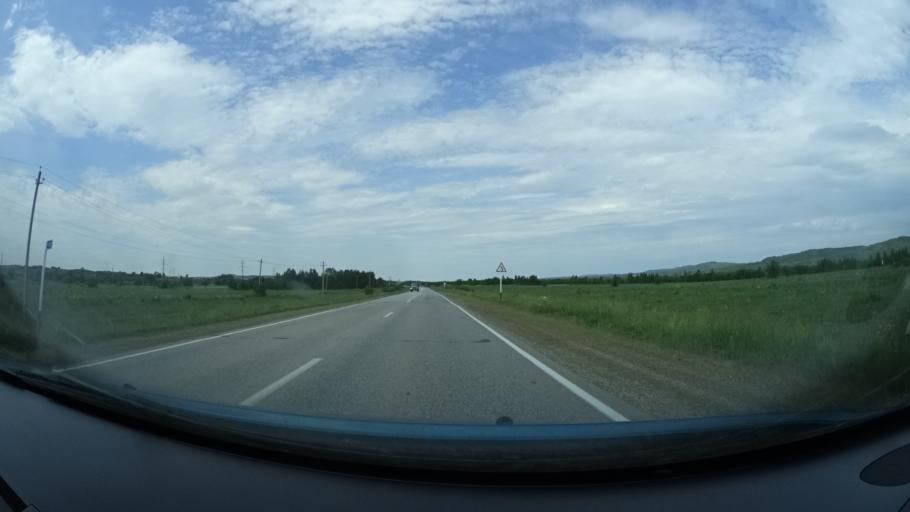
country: RU
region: Perm
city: Barda
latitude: 57.0773
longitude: 55.5429
